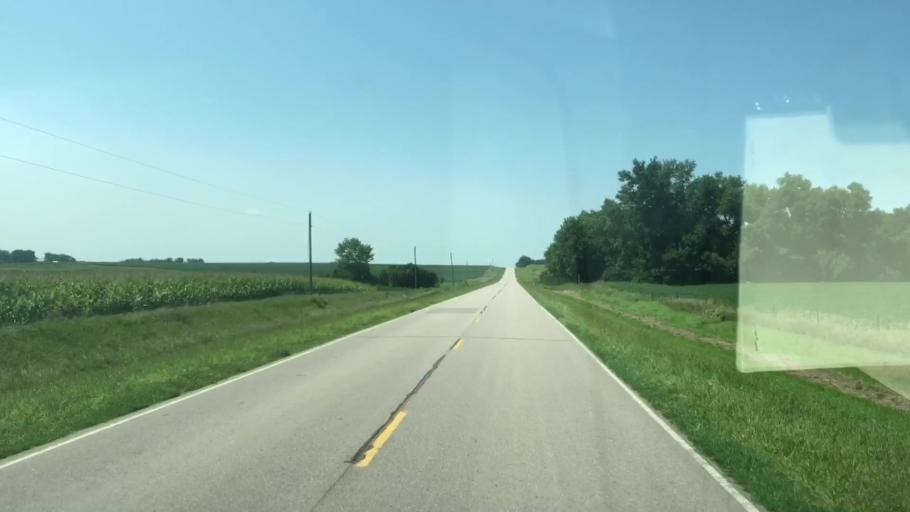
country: US
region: Iowa
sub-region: O'Brien County
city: Sanborn
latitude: 43.2442
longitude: -95.7263
